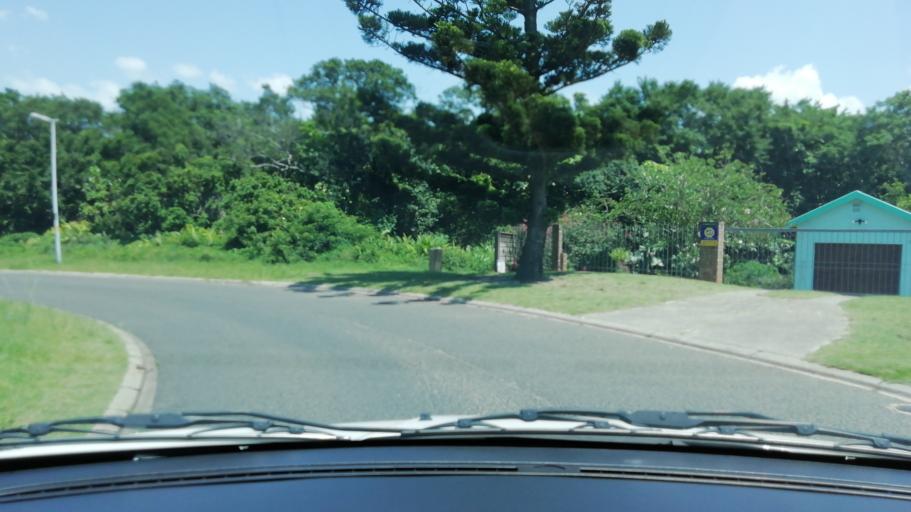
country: ZA
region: KwaZulu-Natal
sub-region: uThungulu District Municipality
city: Richards Bay
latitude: -28.7358
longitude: 32.0569
